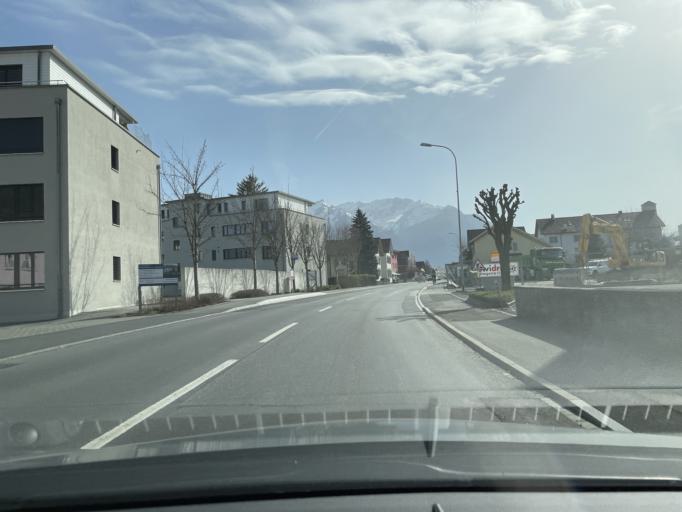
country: CH
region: Saint Gallen
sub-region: Wahlkreis Werdenberg
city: Buchs
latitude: 47.1518
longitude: 9.4815
